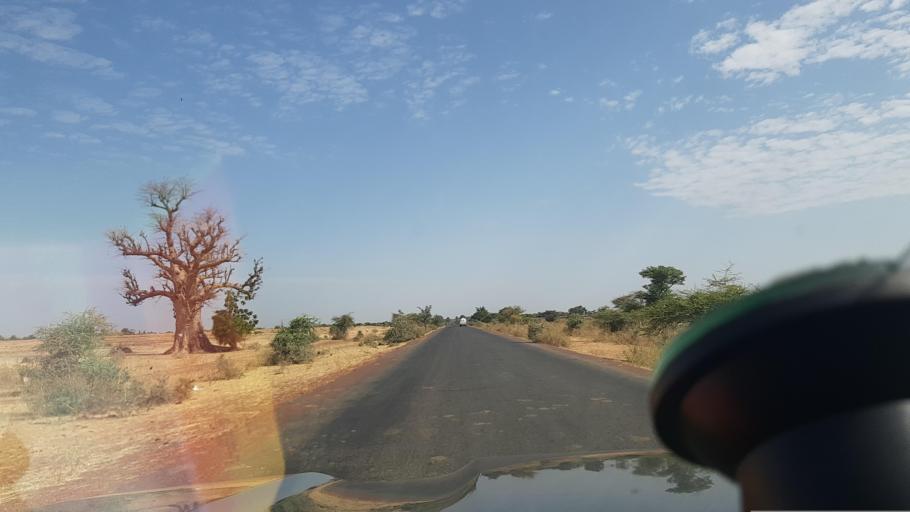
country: ML
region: Segou
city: Markala
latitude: 13.6955
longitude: -6.0980
